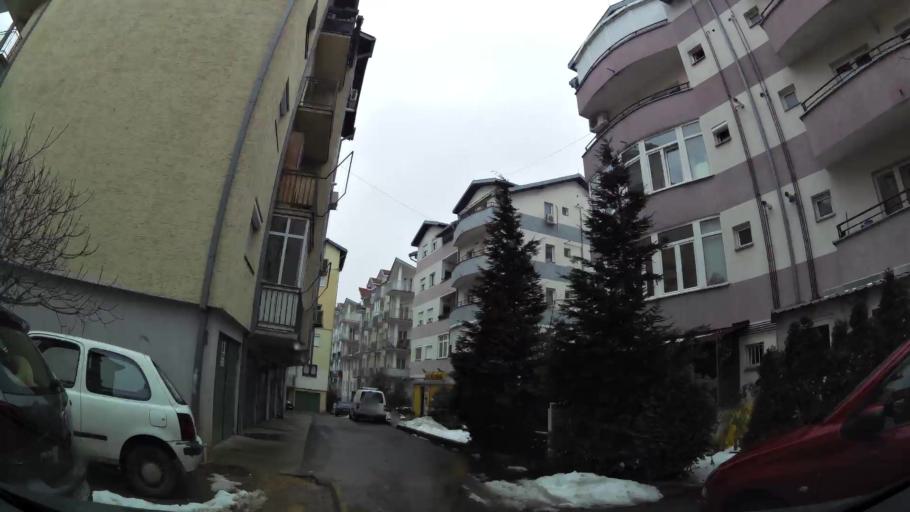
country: RS
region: Central Serbia
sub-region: Belgrade
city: Vozdovac
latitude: 44.7643
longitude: 20.5022
